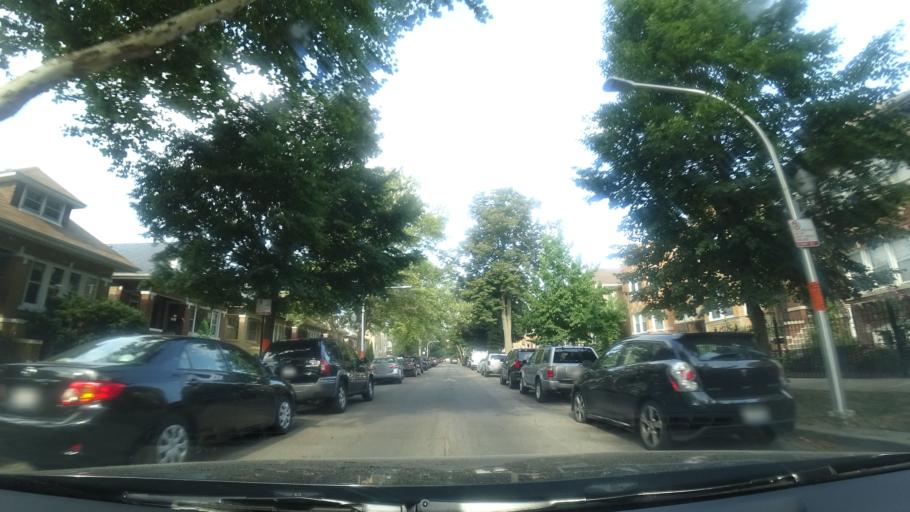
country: US
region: Illinois
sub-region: Cook County
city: Elmwood Park
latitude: 41.9286
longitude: -87.7600
